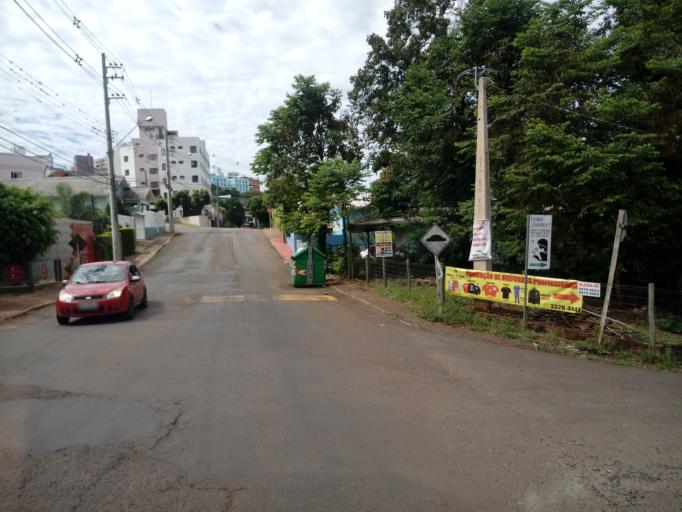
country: BR
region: Santa Catarina
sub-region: Chapeco
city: Chapeco
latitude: -27.0965
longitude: -52.6238
